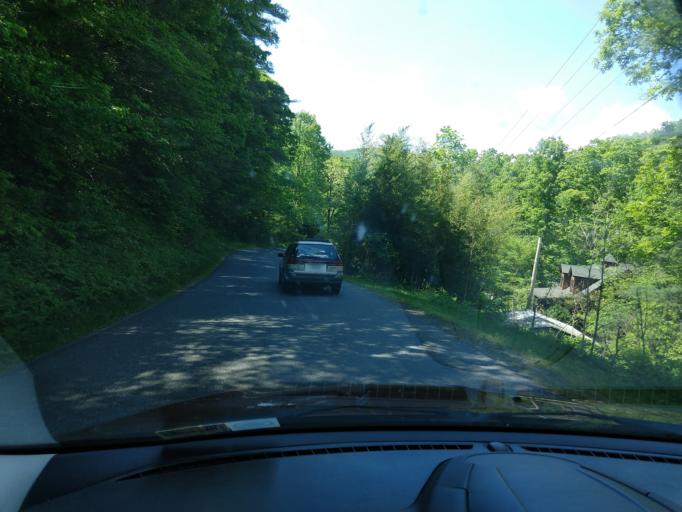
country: US
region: Virginia
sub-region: City of Covington
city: Fairlawn
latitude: 37.6992
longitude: -79.8878
